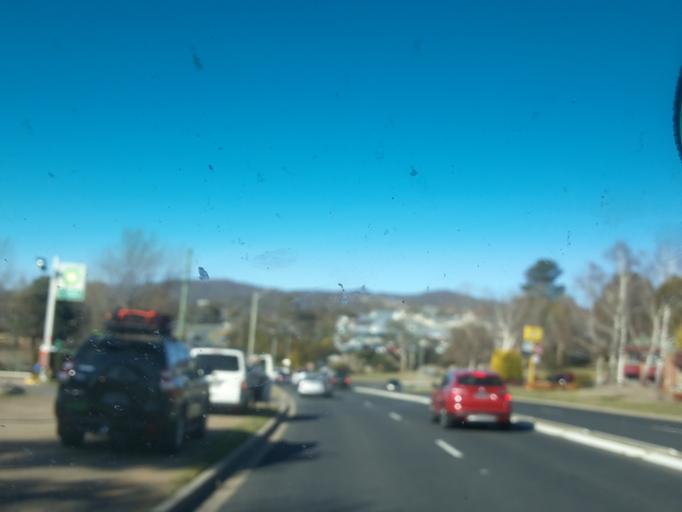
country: AU
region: New South Wales
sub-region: Snowy River
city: Jindabyne
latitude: -36.4152
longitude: 148.6175
